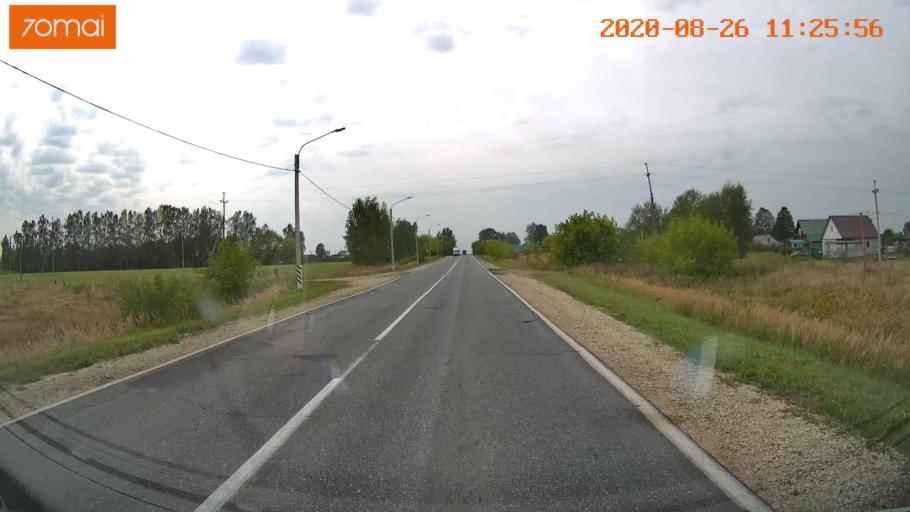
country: RU
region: Rjazan
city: Shilovo
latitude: 54.3375
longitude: 40.9559
